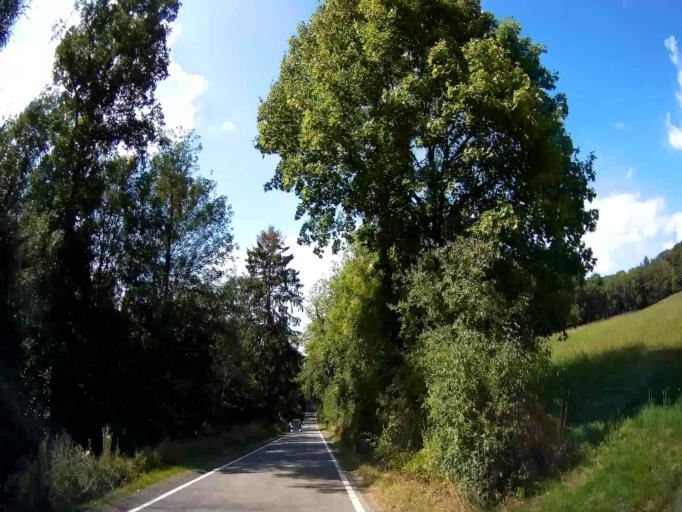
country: BE
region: Wallonia
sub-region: Province de Namur
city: Yvoir
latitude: 50.3510
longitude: 4.9380
